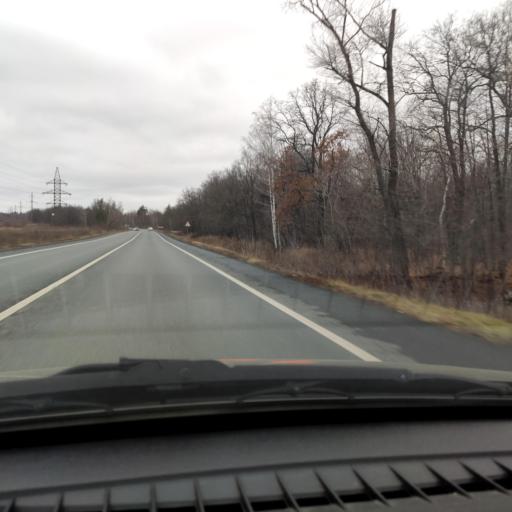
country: RU
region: Samara
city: Pribrezhnyy
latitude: 53.5083
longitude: 49.9342
